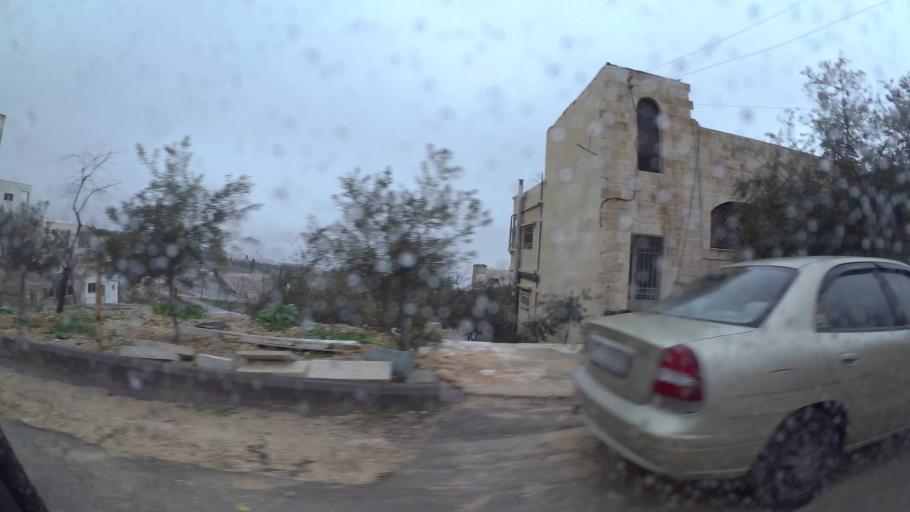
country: JO
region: Amman
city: Al Jubayhah
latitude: 32.0363
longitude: 35.8504
